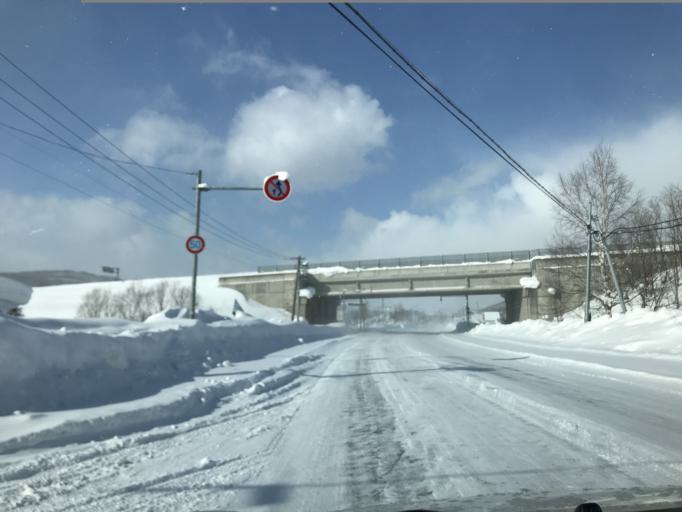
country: JP
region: Hokkaido
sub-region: Asahikawa-shi
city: Asahikawa
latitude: 43.9219
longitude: 142.4781
